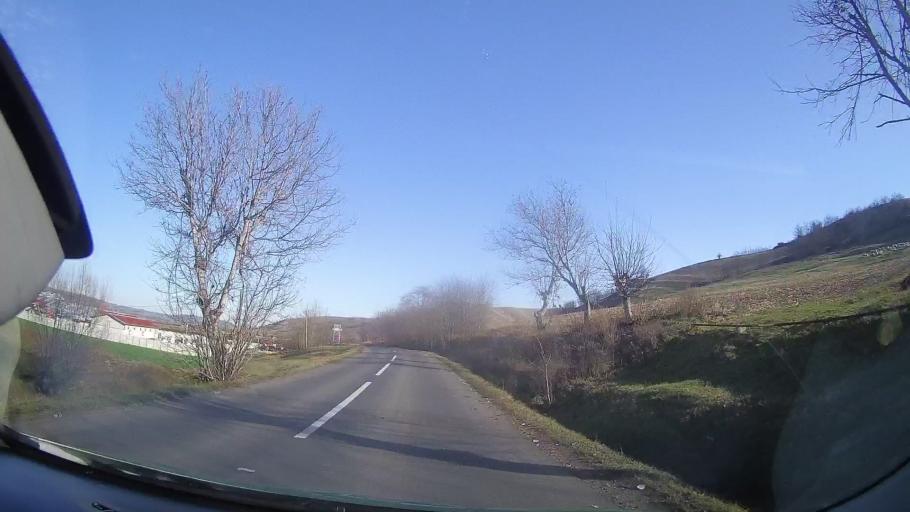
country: RO
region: Mures
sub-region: Comuna Iclanzel
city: Iclanzel
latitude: 46.5492
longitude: 24.3275
